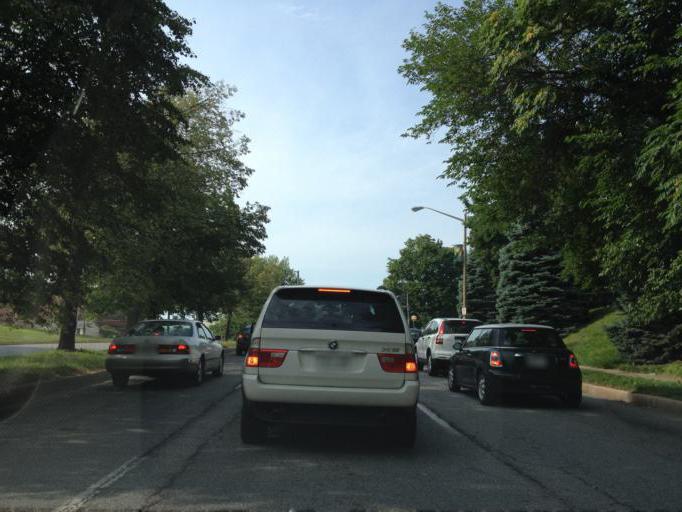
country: US
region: Maryland
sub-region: Baltimore County
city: Towson
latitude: 39.4046
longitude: -76.6083
